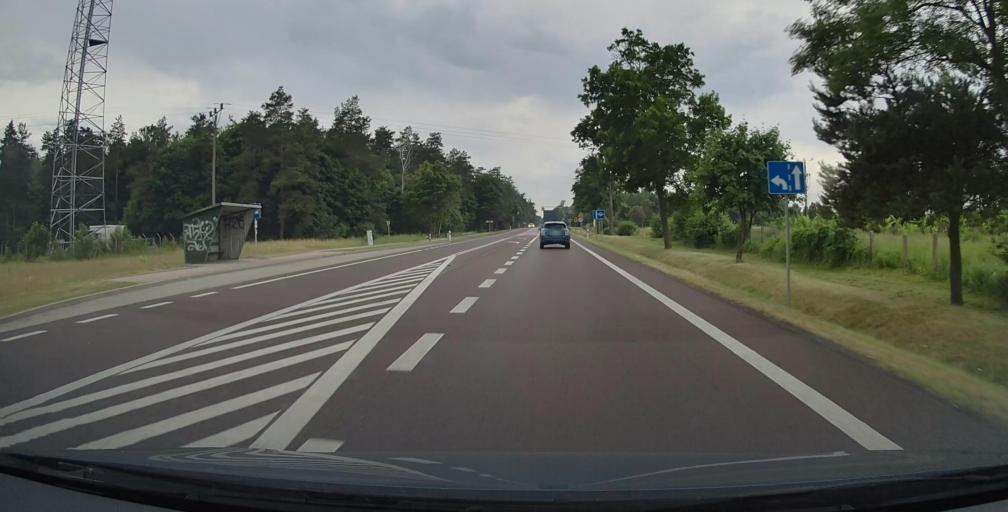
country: PL
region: Lublin Voivodeship
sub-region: Powiat bialski
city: Lesna Podlaska
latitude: 52.0373
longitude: 22.9362
